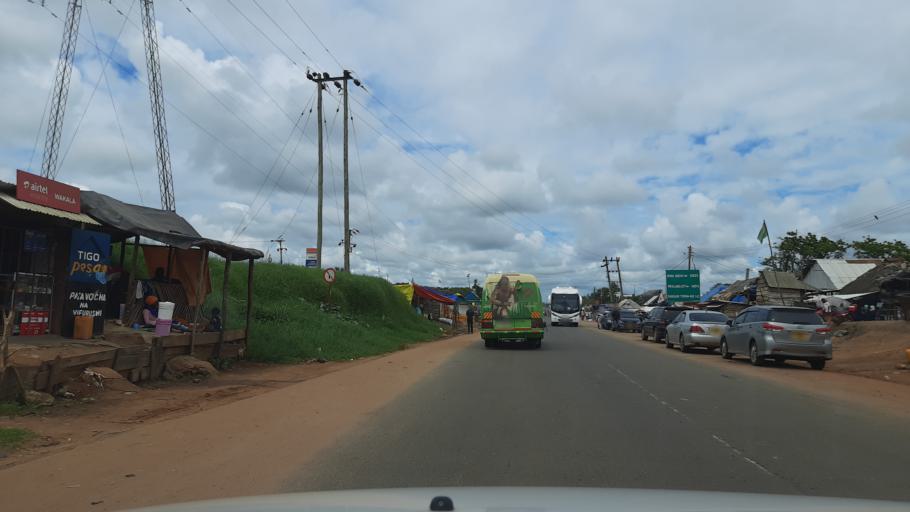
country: TZ
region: Tanga
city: Chanika
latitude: -5.7869
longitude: 38.2909
